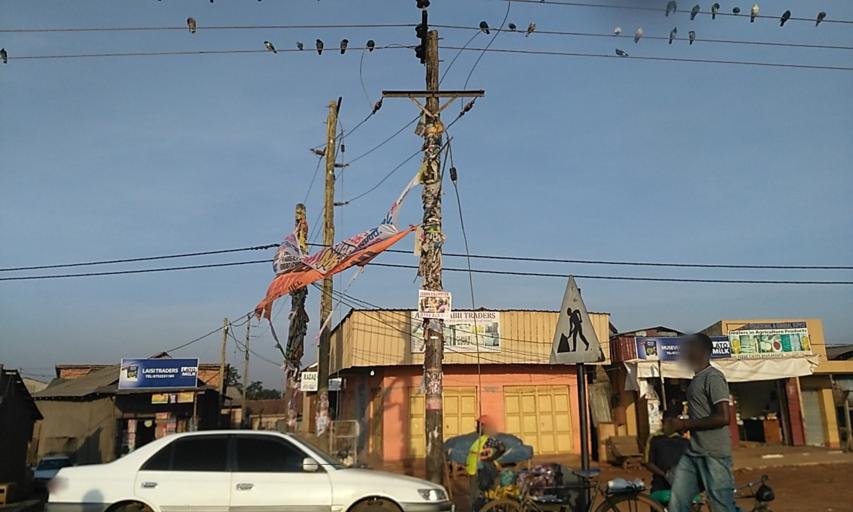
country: UG
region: Central Region
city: Kampala Central Division
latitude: 0.3510
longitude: 32.5714
